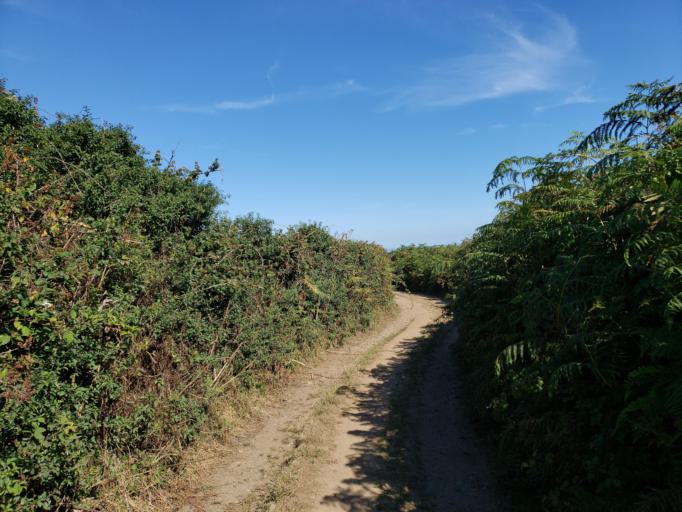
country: GB
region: England
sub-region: Cornwall
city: St Ives
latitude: 50.2115
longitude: -5.5024
